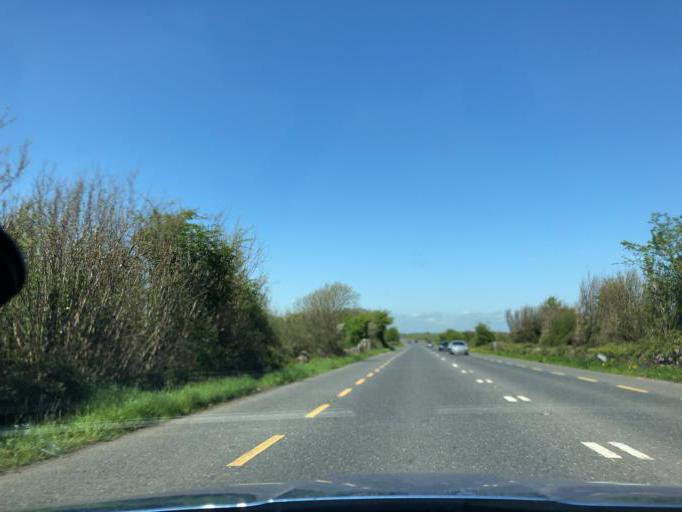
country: IE
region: Connaught
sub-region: County Galway
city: Athenry
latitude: 53.2404
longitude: -8.7535
